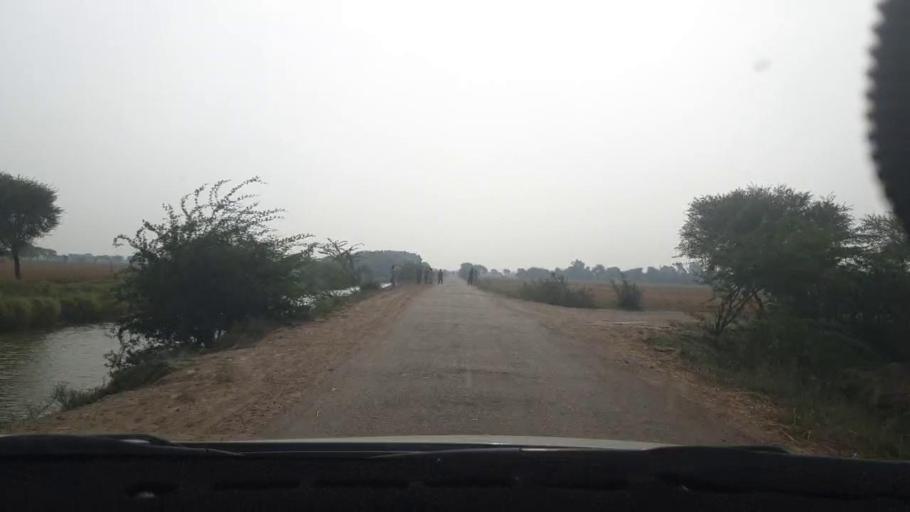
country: PK
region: Sindh
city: Tando Muhammad Khan
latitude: 25.0613
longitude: 68.5436
